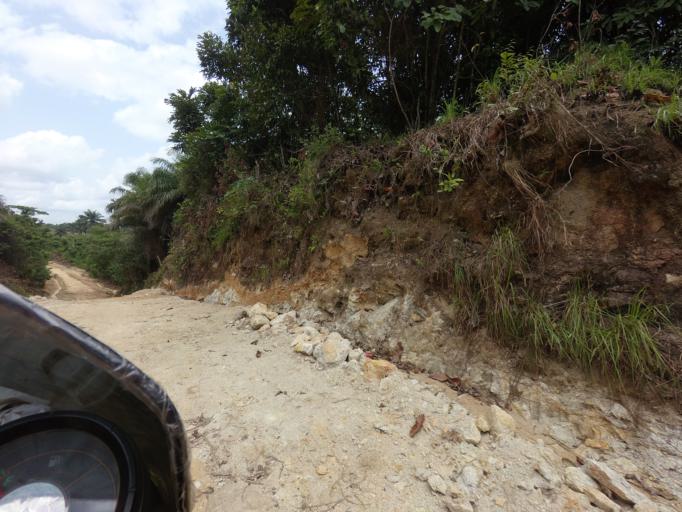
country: SL
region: Eastern Province
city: Kailahun
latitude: 8.3647
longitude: -10.7162
